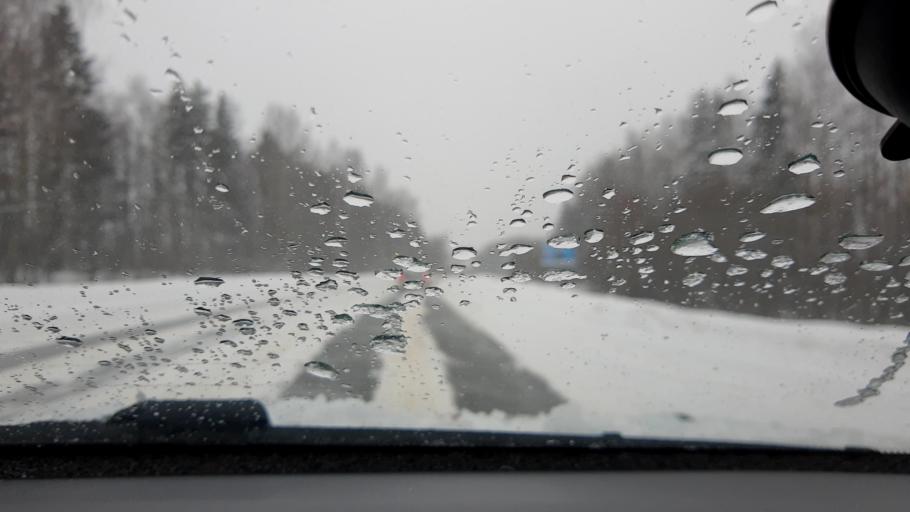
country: RU
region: Nizjnij Novgorod
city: Pervomayskiy
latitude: 56.6277
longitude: 43.2391
